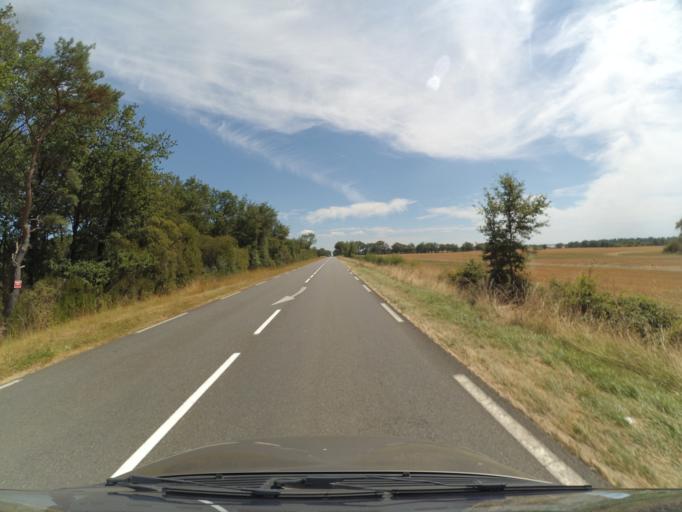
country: FR
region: Poitou-Charentes
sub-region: Departement de la Charente
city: Confolens
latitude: 46.0595
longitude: 0.6069
